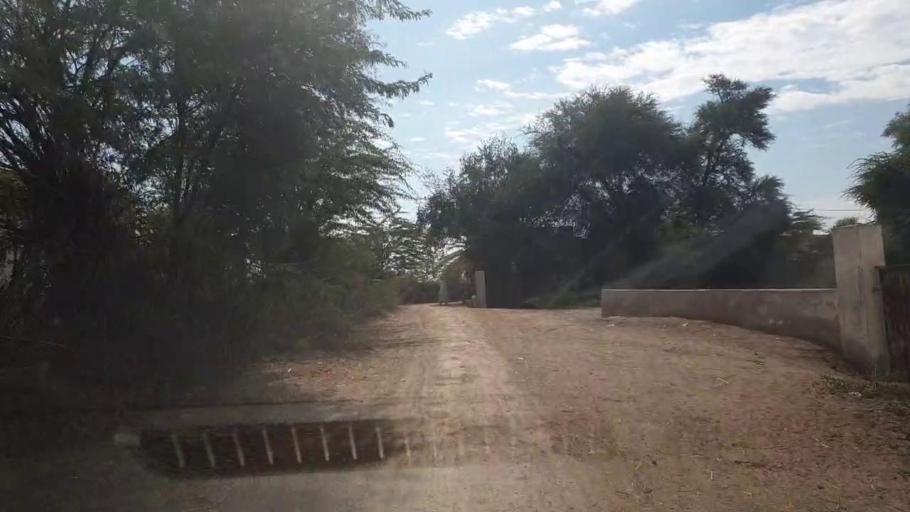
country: PK
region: Sindh
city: Sanghar
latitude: 26.0420
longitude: 68.9255
